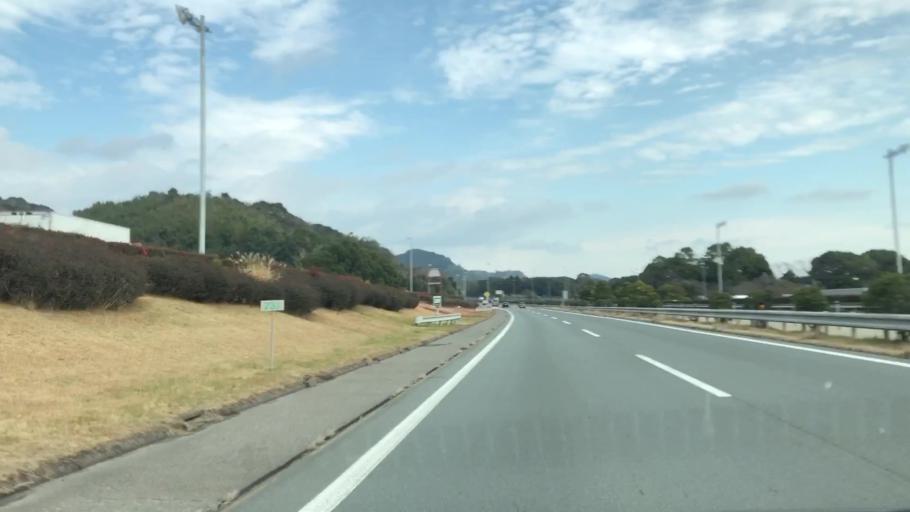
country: JP
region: Saga Prefecture
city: Kanzakimachi-kanzaki
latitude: 33.3292
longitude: 130.3112
